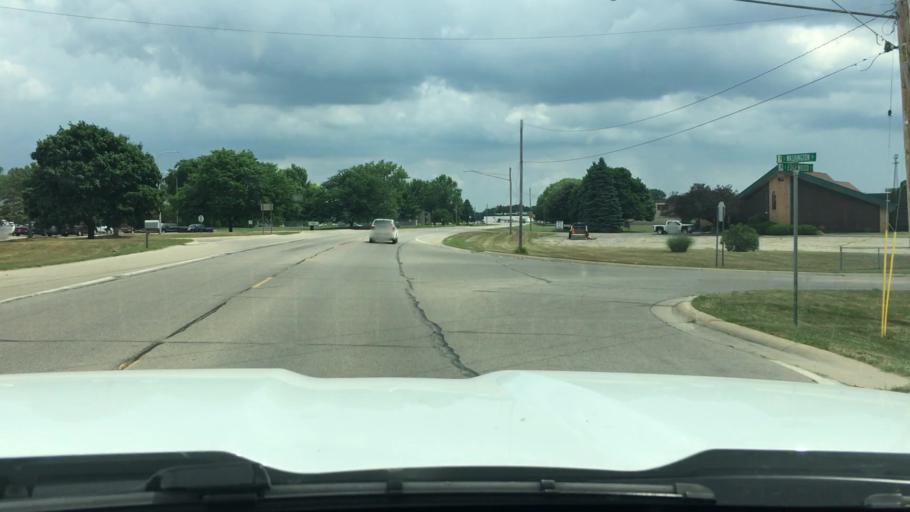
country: US
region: Michigan
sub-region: Montcalm County
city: Greenville
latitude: 43.1757
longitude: -85.2382
